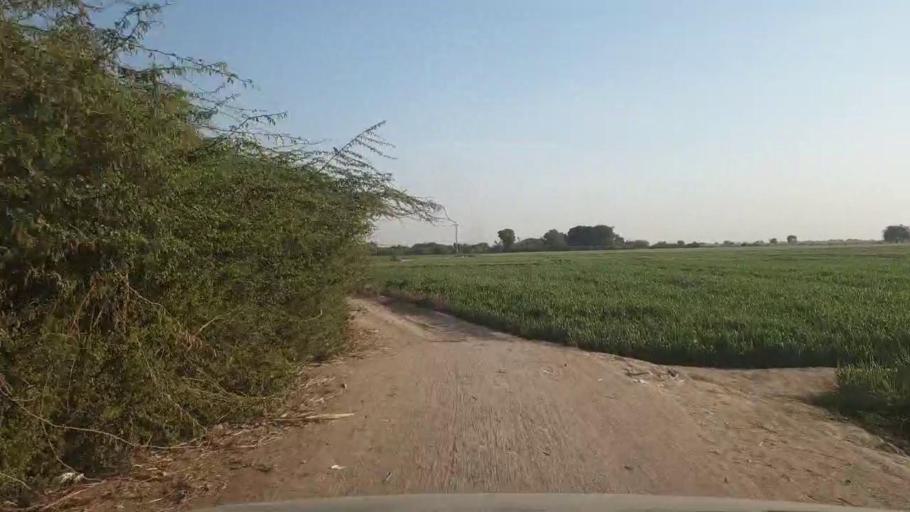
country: PK
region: Sindh
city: Chambar
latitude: 25.2509
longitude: 68.8851
